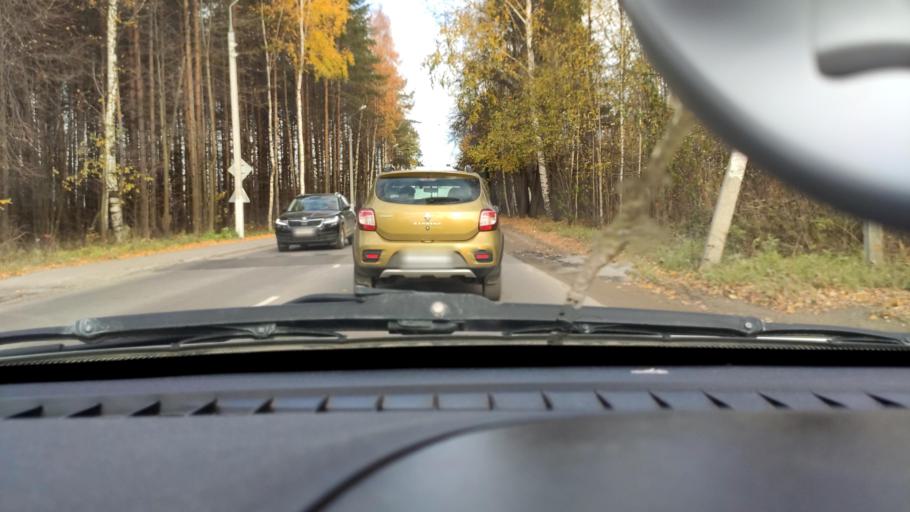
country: RU
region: Perm
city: Perm
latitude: 58.0925
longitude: 56.4039
